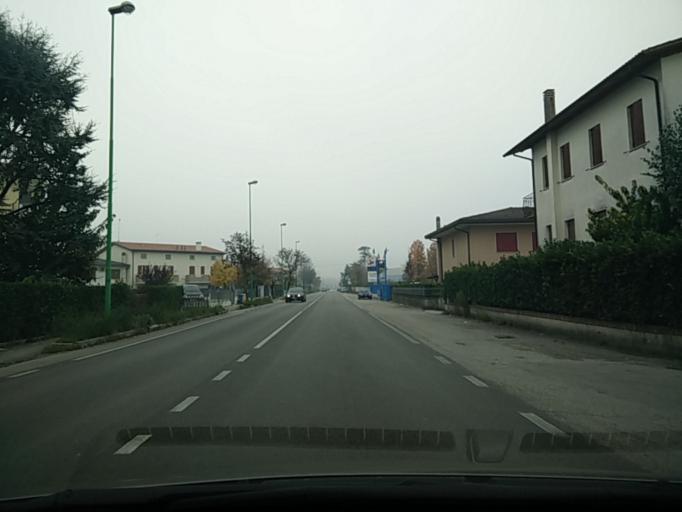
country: IT
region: Veneto
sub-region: Provincia di Venezia
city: Salzano
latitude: 45.5237
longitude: 12.0907
